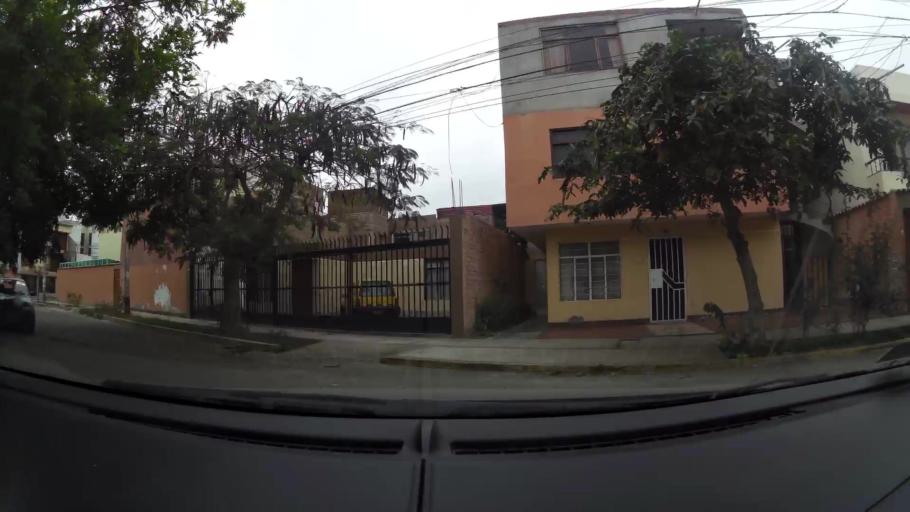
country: PE
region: La Libertad
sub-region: Provincia de Trujillo
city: Trujillo
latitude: -8.1030
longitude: -79.0404
